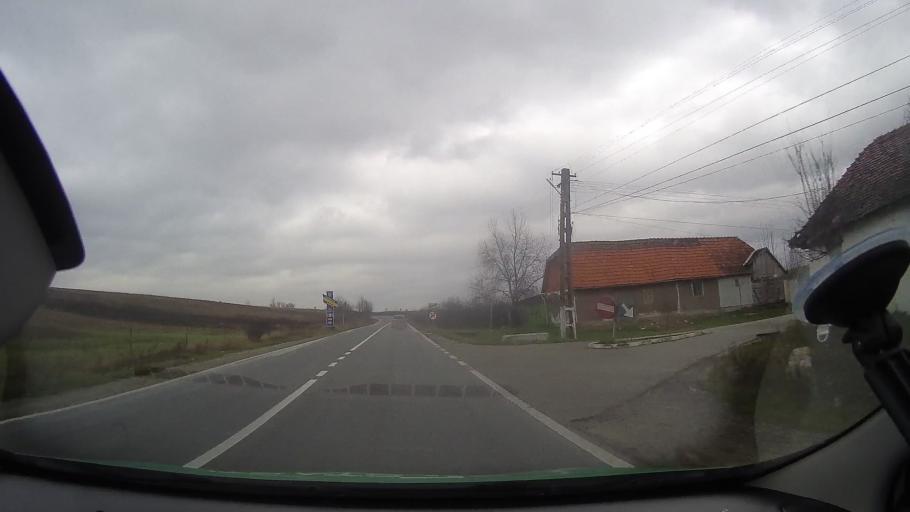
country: RO
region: Arad
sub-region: Comuna Almas
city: Almas
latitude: 46.2835
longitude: 22.2411
